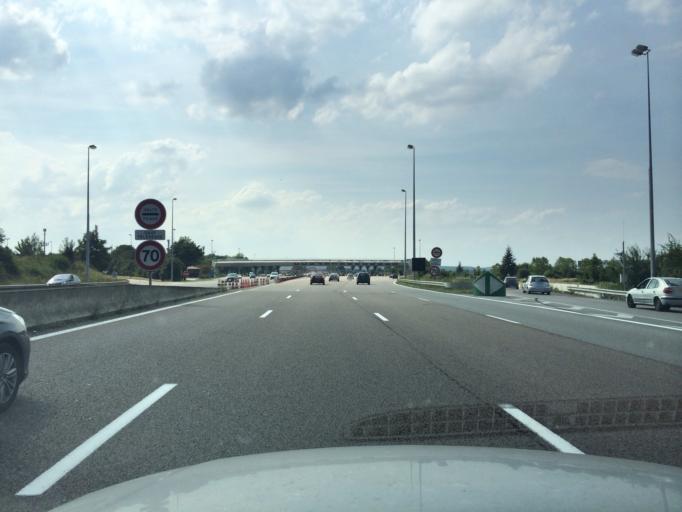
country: FR
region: Ile-de-France
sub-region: Departement des Yvelines
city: Buchelay
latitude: 48.9828
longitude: 1.6860
